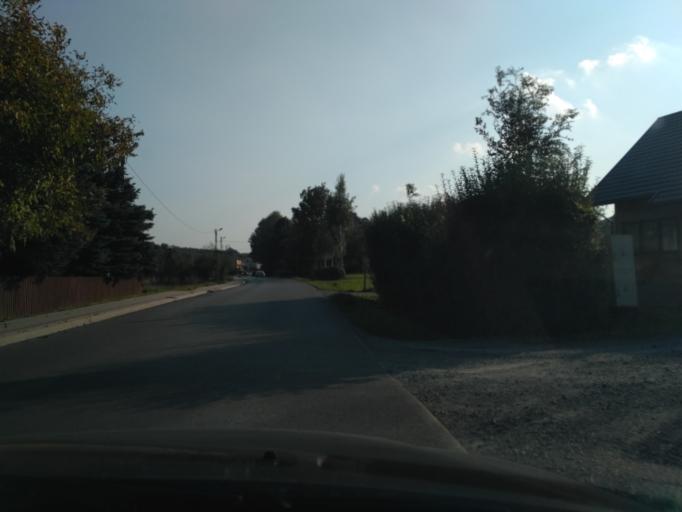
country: PL
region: Subcarpathian Voivodeship
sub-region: Powiat rzeszowski
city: Niechobrz
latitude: 49.9876
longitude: 21.8750
